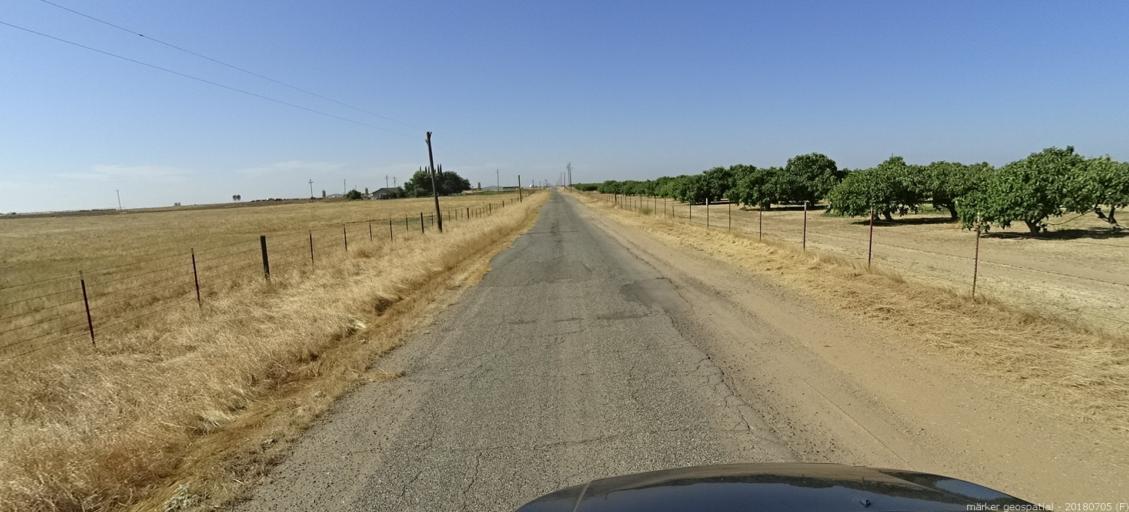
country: US
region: California
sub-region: Madera County
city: Madera Acres
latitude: 37.1541
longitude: -120.0748
